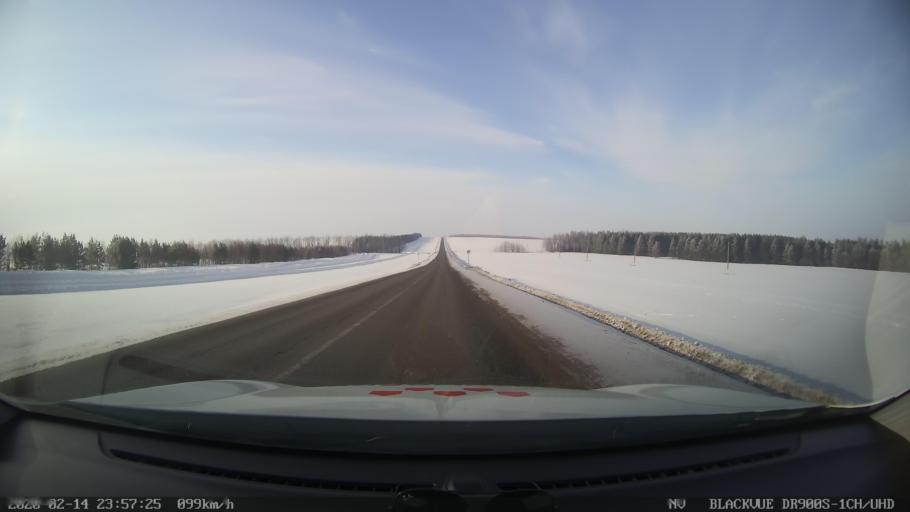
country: RU
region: Tatarstan
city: Kuybyshevskiy Zaton
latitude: 55.3339
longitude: 49.1098
